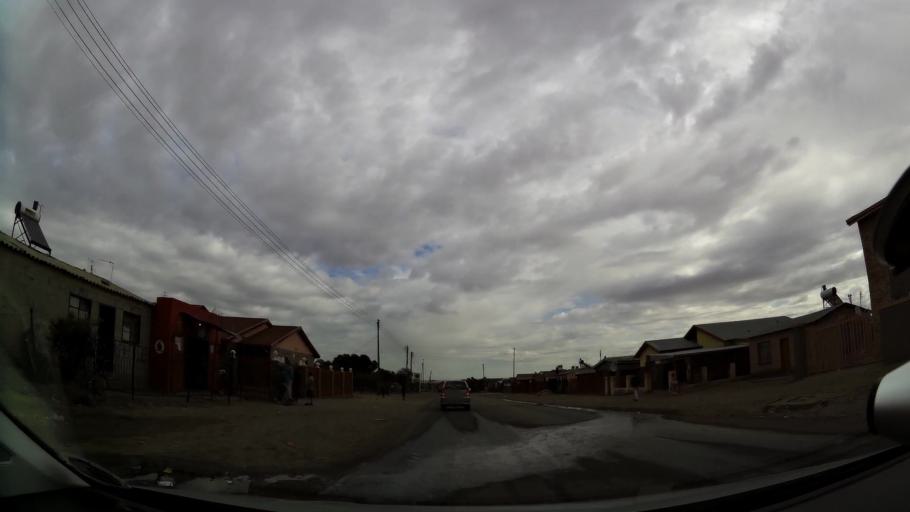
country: ZA
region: Orange Free State
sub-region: Fezile Dabi District Municipality
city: Kroonstad
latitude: -27.6435
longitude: 27.1835
